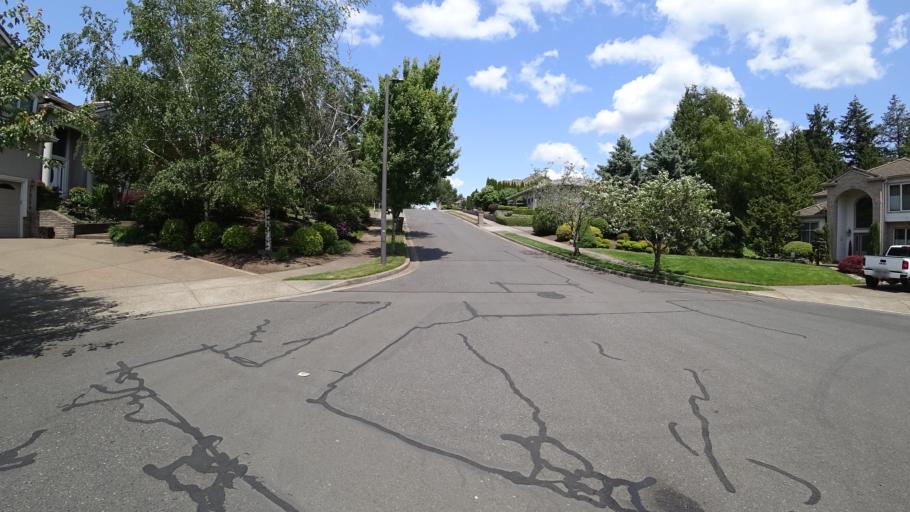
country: US
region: Oregon
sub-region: Clackamas County
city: Happy Valley
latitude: 45.4493
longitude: -122.5456
